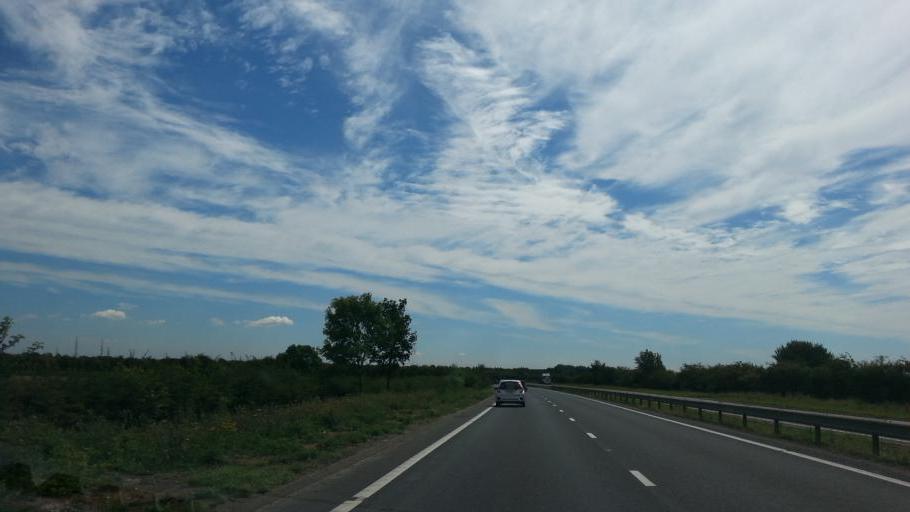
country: GB
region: England
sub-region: Cambridgeshire
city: Waterbeach
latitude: 52.2220
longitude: 0.1870
